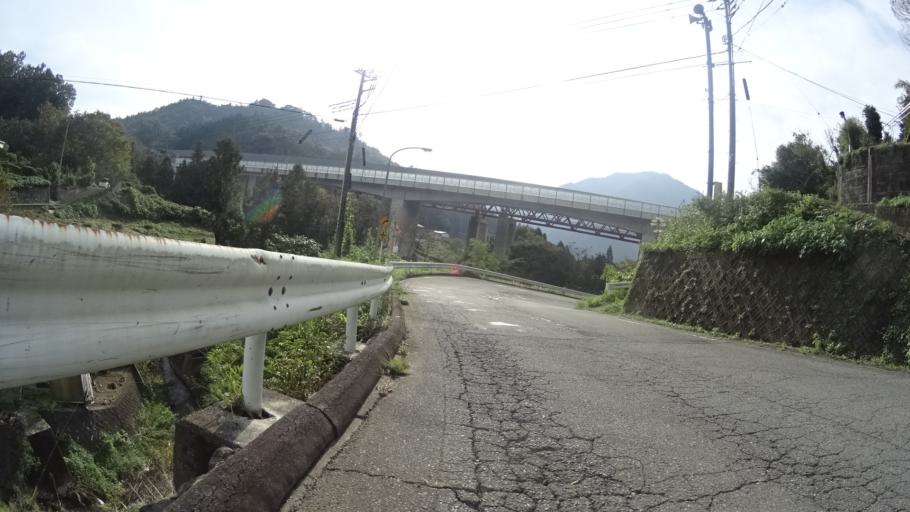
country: JP
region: Yamanashi
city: Otsuki
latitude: 35.6117
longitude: 139.0130
